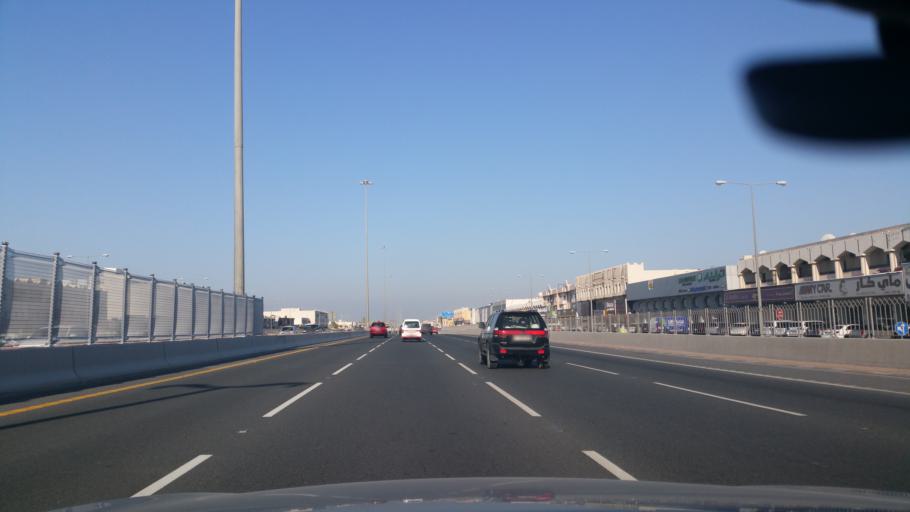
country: QA
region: Baladiyat ar Rayyan
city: Ar Rayyan
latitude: 25.2299
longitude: 51.4399
